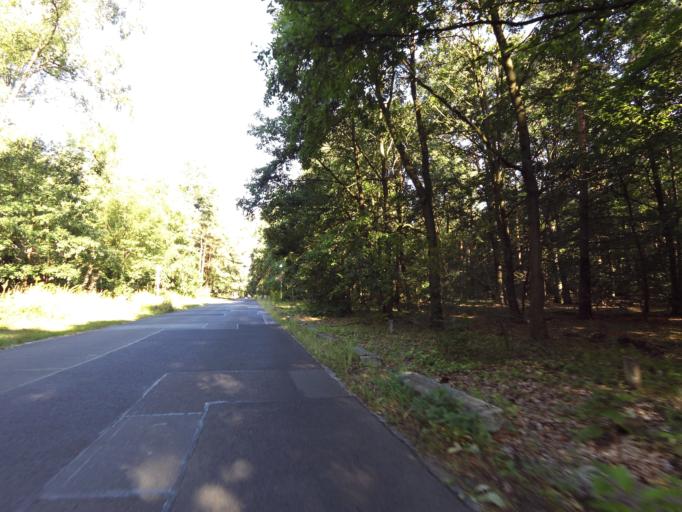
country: DE
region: Berlin
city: Nikolassee
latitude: 52.4354
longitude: 13.1856
